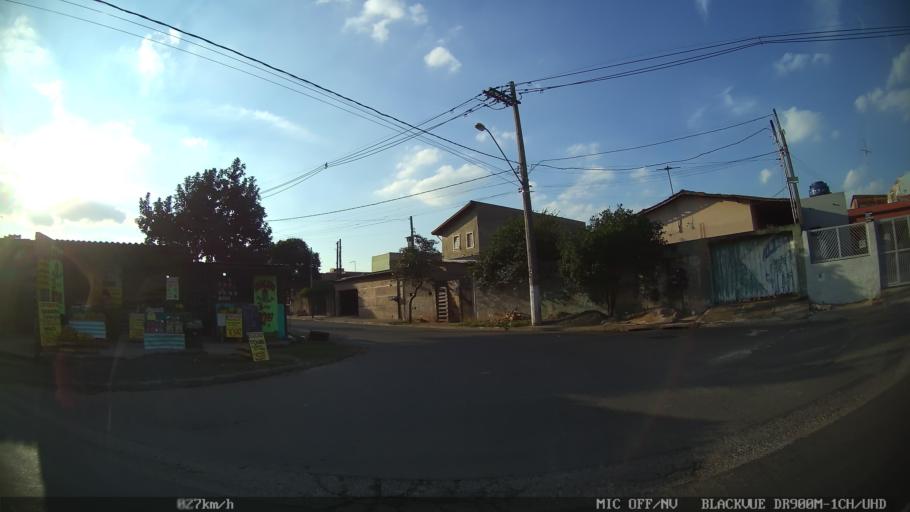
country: BR
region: Sao Paulo
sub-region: Hortolandia
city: Hortolandia
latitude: -22.8597
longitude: -47.1580
